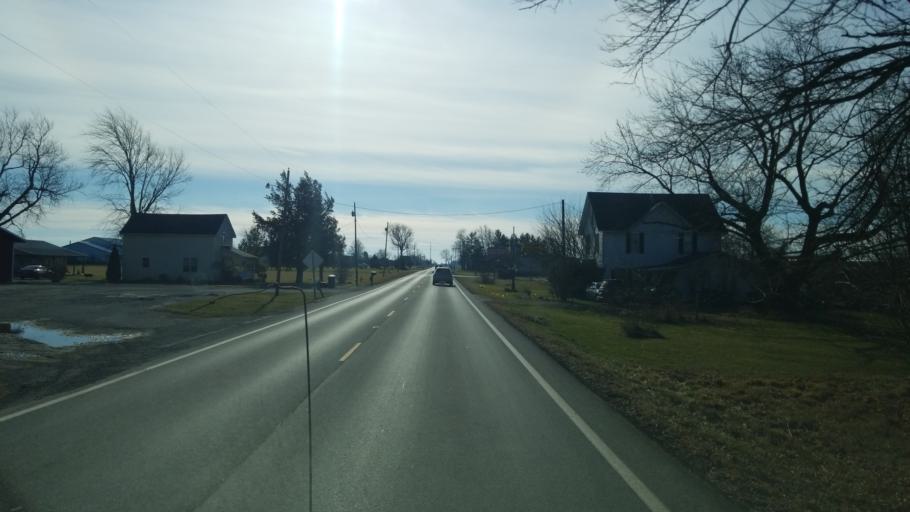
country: US
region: Ohio
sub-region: Putnam County
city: Leipsic
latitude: 41.0926
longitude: -83.9864
